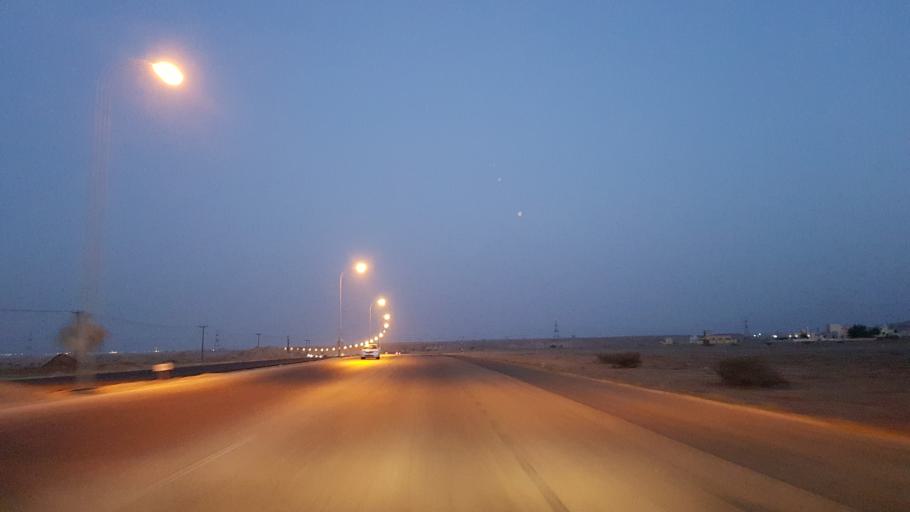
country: OM
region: Ash Sharqiyah
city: Sur
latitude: 22.5924
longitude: 59.4378
